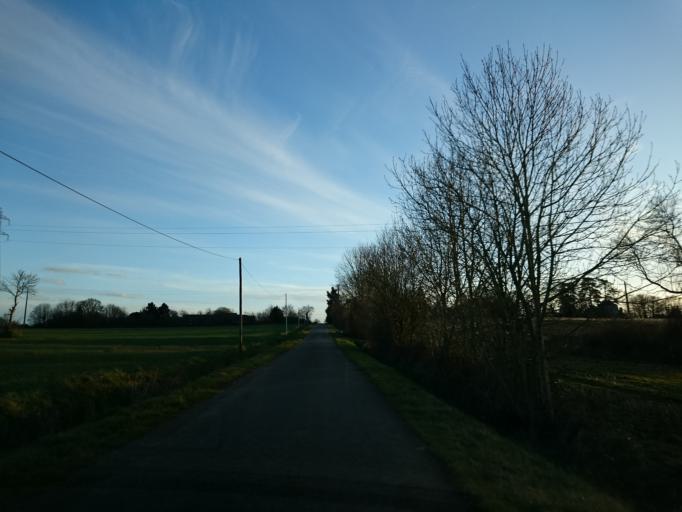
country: FR
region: Brittany
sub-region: Departement d'Ille-et-Vilaine
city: Chanteloup
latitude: 47.9173
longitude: -1.6065
